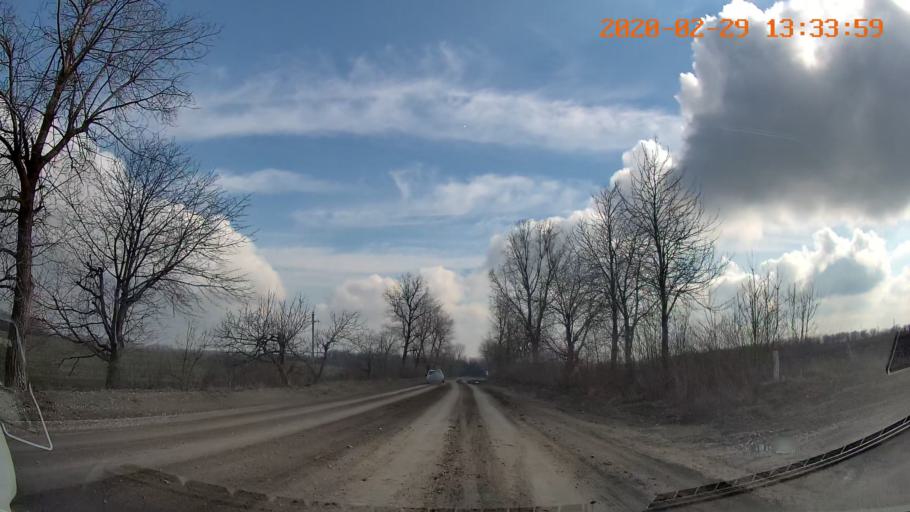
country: MD
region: Telenesti
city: Camenca
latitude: 47.8710
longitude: 28.6198
